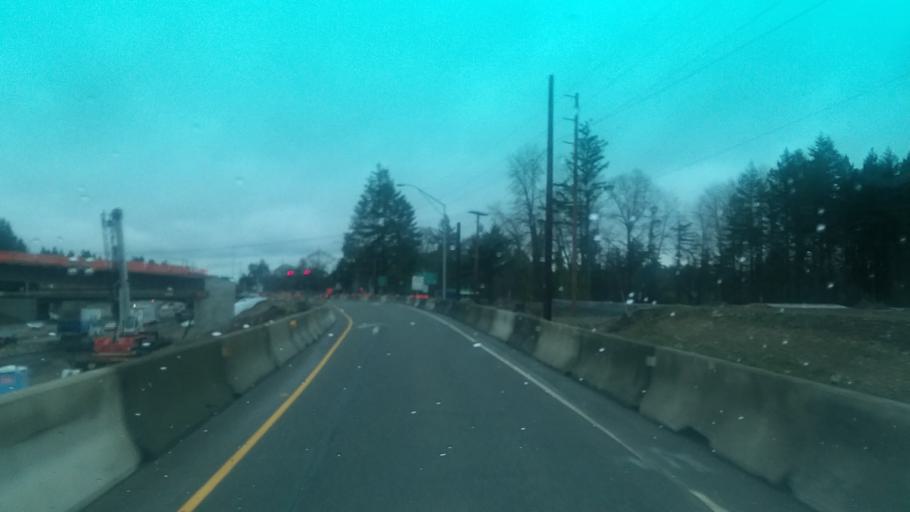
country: US
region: Washington
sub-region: Pierce County
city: Fort Lewis
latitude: 47.1257
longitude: -122.5441
